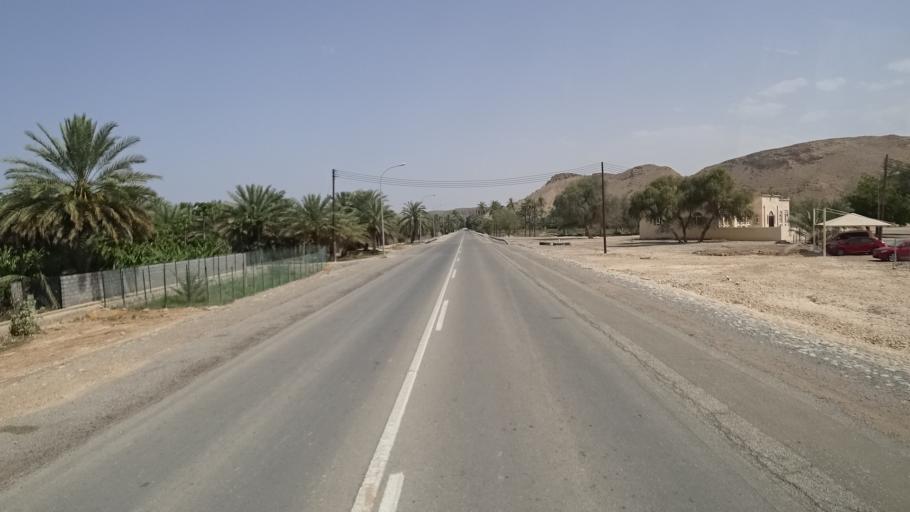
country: OM
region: Muhafazat Masqat
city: Muscat
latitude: 23.1724
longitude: 58.9138
